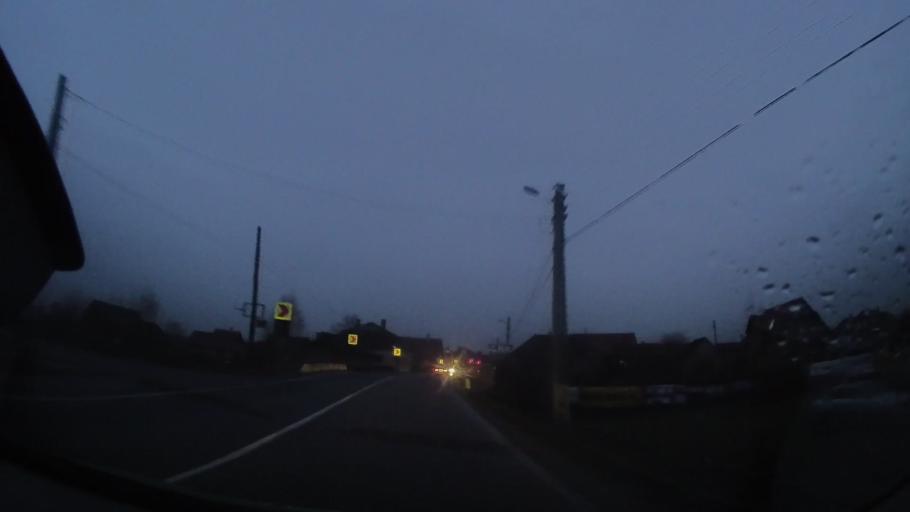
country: RO
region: Harghita
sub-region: Comuna Ditrau
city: Ditrau
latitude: 46.8072
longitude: 25.4930
